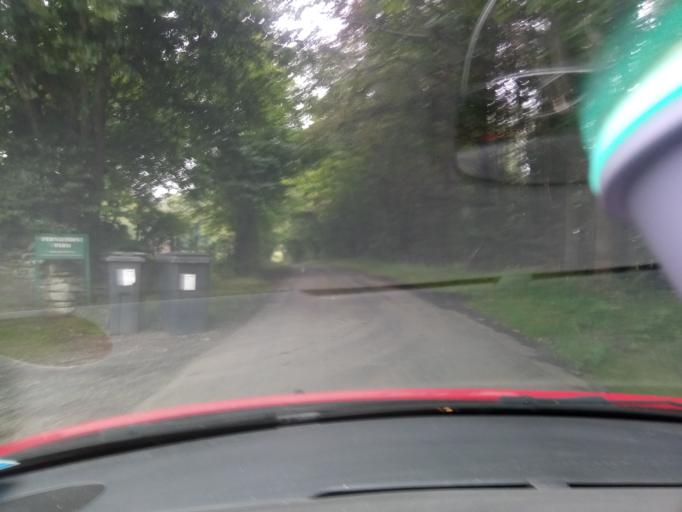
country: GB
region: Scotland
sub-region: The Scottish Borders
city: Galashiels
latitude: 55.6648
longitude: -2.8801
